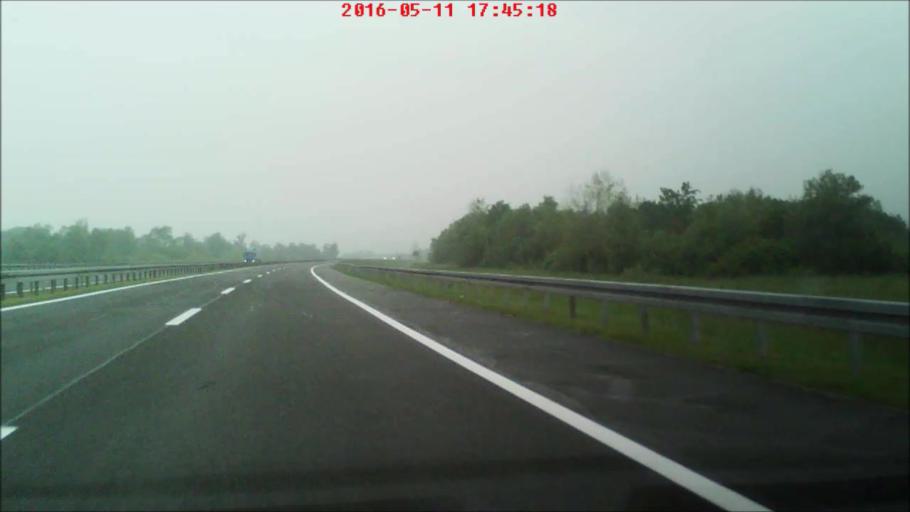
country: HR
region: Zagrebacka
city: Jakovlje
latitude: 45.9682
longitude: 15.8504
